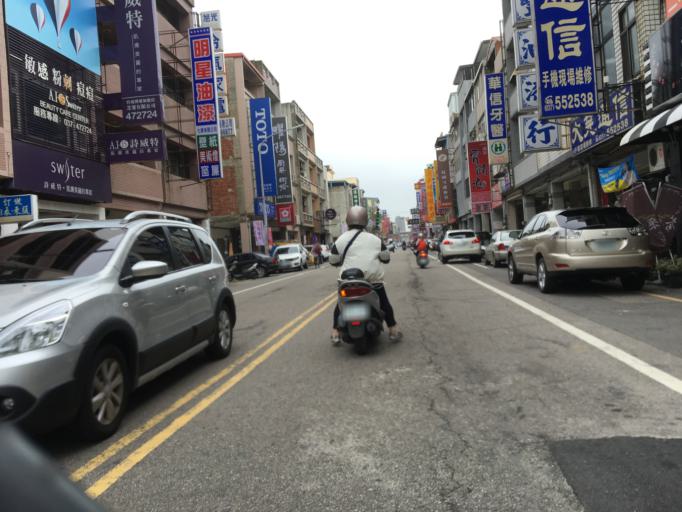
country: TW
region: Taiwan
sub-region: Miaoli
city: Miaoli
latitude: 24.6870
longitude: 120.8731
